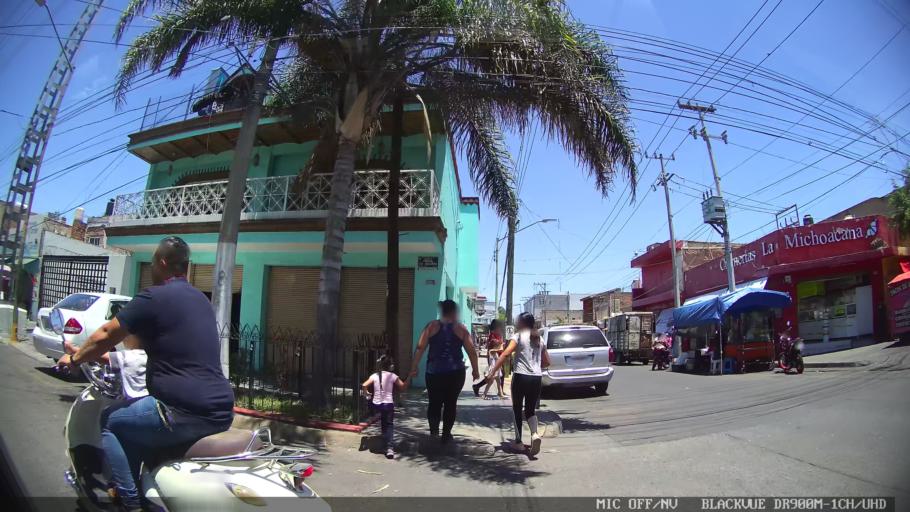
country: MX
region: Jalisco
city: Tlaquepaque
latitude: 20.6721
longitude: -103.2763
